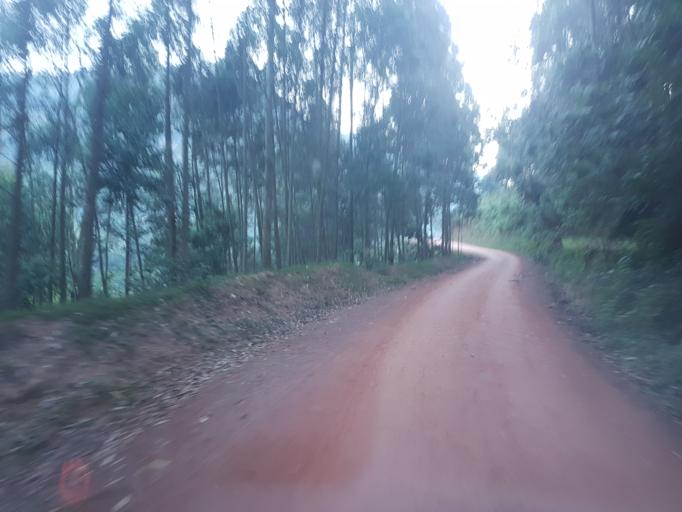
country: UG
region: Western Region
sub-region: Kanungu District
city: Kanungu
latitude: -0.9481
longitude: 29.8253
